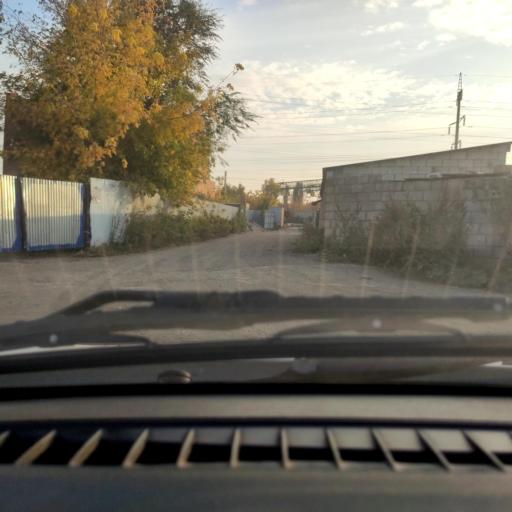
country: RU
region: Samara
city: Tol'yatti
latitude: 53.5281
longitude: 49.4653
